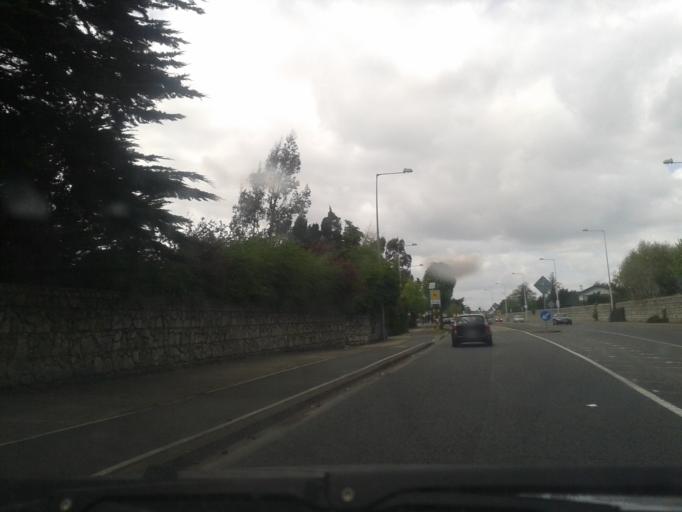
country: IE
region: Leinster
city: Sallynoggin
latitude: 53.2638
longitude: -6.1321
